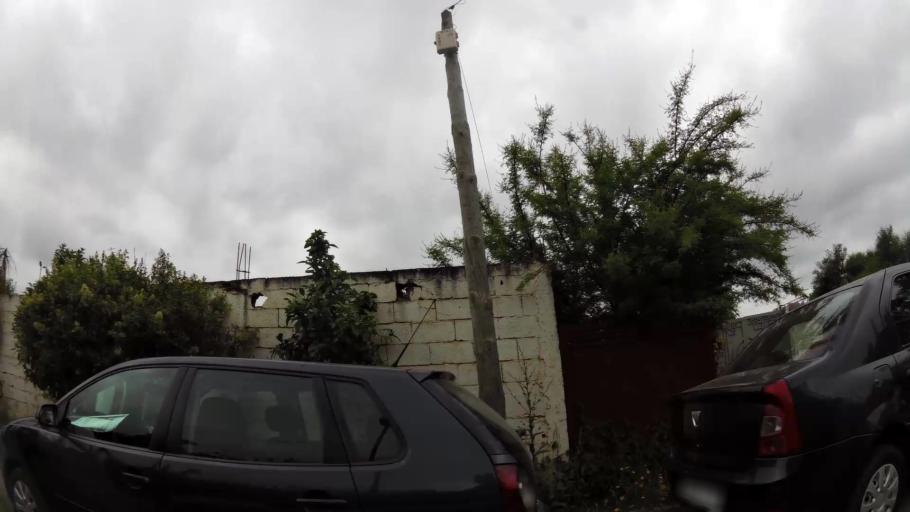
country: MA
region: Rabat-Sale-Zemmour-Zaer
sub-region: Rabat
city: Rabat
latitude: 33.9618
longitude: -6.8243
